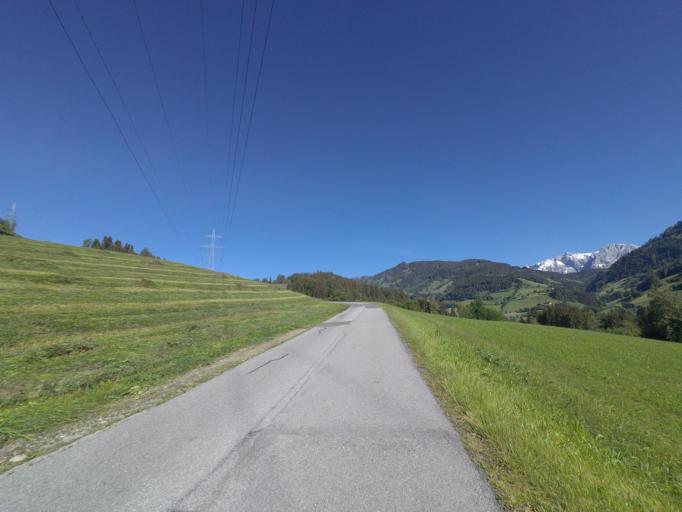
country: AT
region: Salzburg
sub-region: Politischer Bezirk Sankt Johann im Pongau
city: Sankt Veit im Pongau
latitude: 47.3244
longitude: 13.1308
